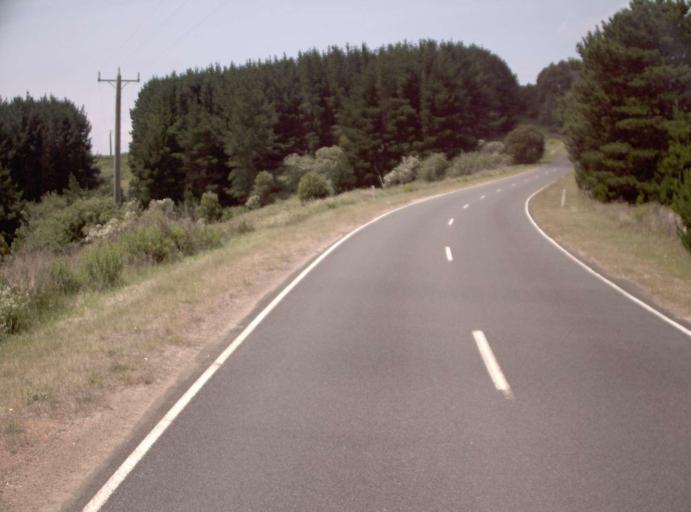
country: AU
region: Victoria
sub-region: Latrobe
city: Traralgon
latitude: -38.3605
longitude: 146.7042
